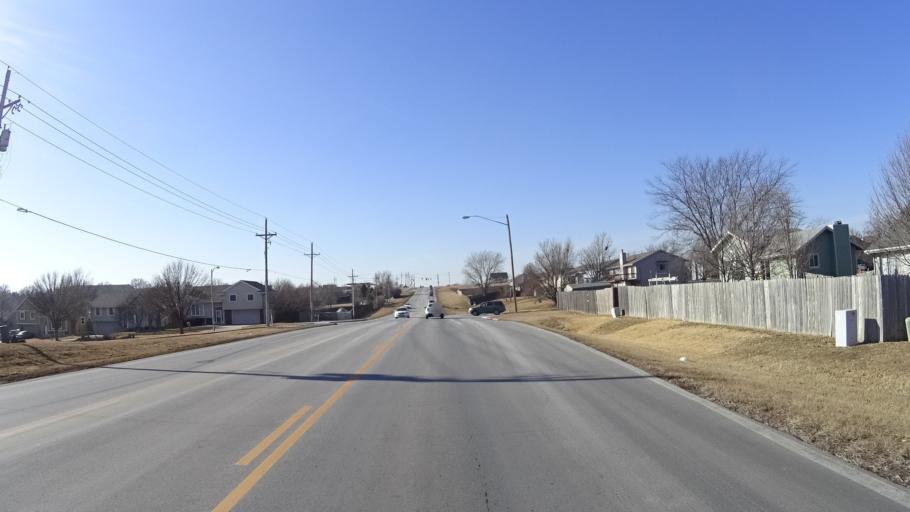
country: US
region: Nebraska
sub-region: Douglas County
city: Bennington
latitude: 41.3067
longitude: -96.1142
